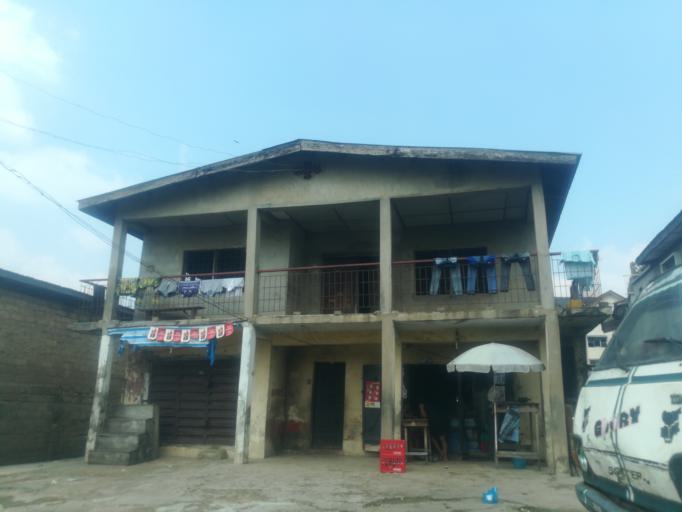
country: NG
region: Oyo
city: Ibadan
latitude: 7.3966
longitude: 3.9082
